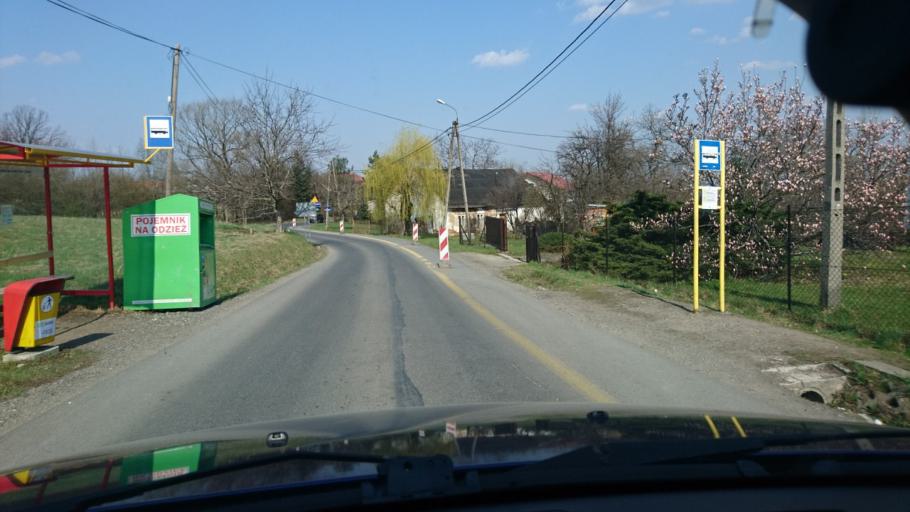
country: PL
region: Silesian Voivodeship
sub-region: Powiat bielski
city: Kozy
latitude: 49.8218
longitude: 19.1164
